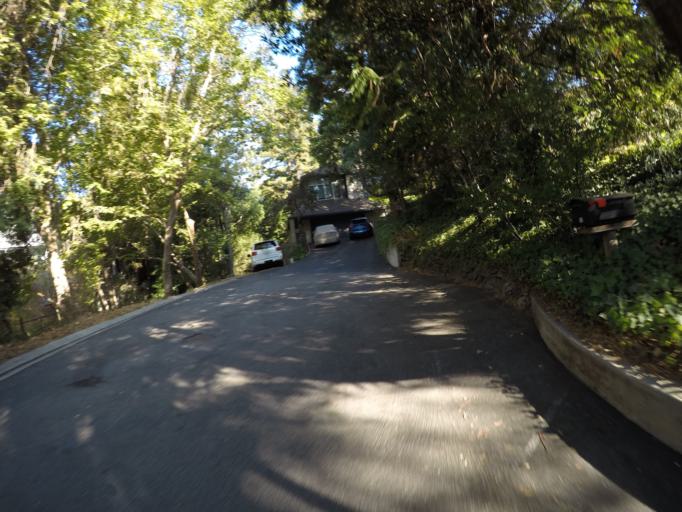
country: US
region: California
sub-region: Santa Cruz County
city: Scotts Valley
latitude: 37.0386
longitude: -122.0198
